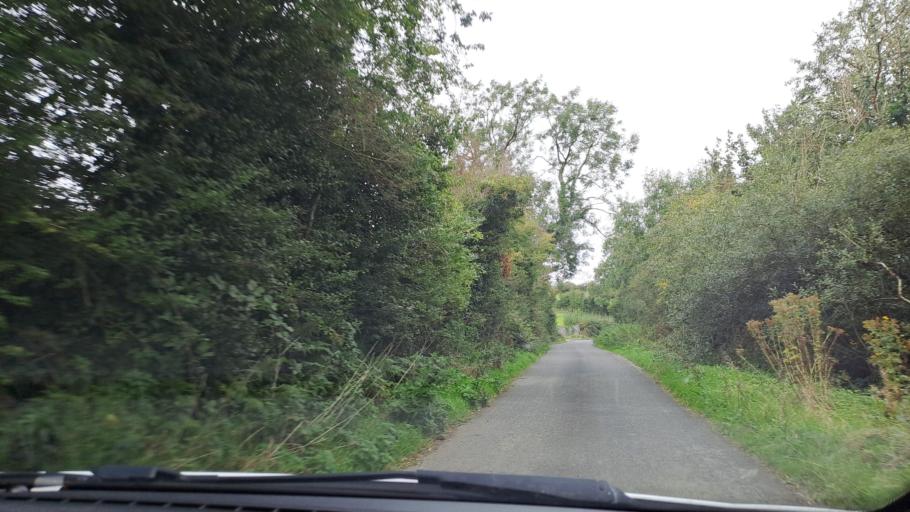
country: IE
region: Ulster
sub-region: An Cabhan
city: Kingscourt
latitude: 53.9686
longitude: -6.8516
